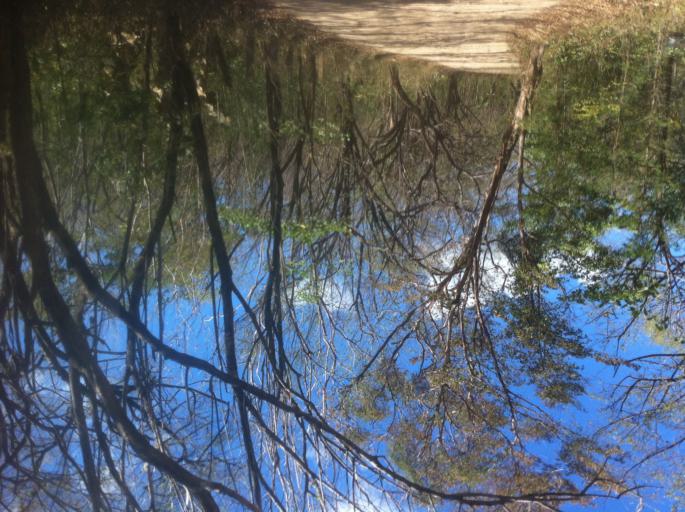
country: NI
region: Rivas
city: Tola
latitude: 11.3861
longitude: -86.0200
